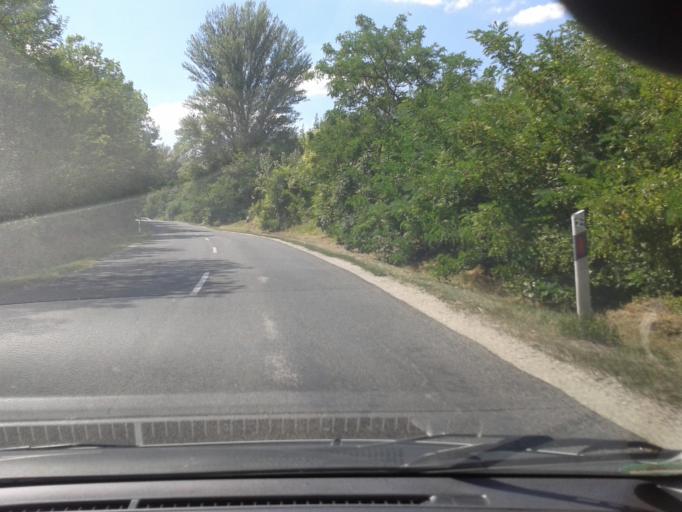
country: HU
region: Pest
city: Szob
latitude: 47.8143
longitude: 18.8227
